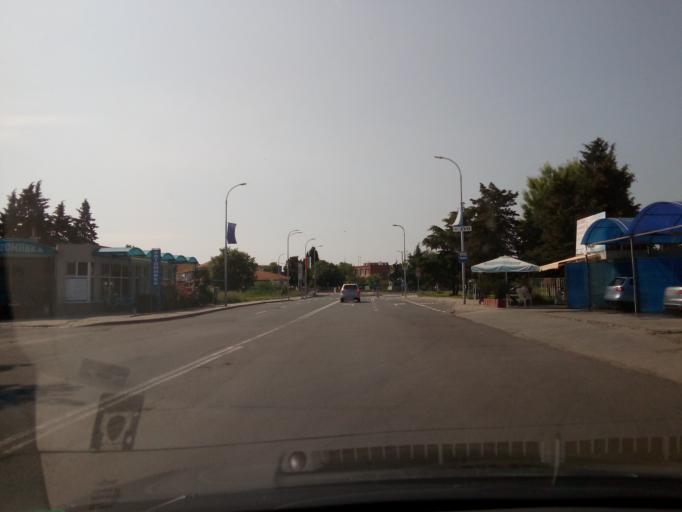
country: BG
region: Burgas
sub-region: Obshtina Pomorie
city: Pomorie
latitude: 42.5682
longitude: 27.6185
